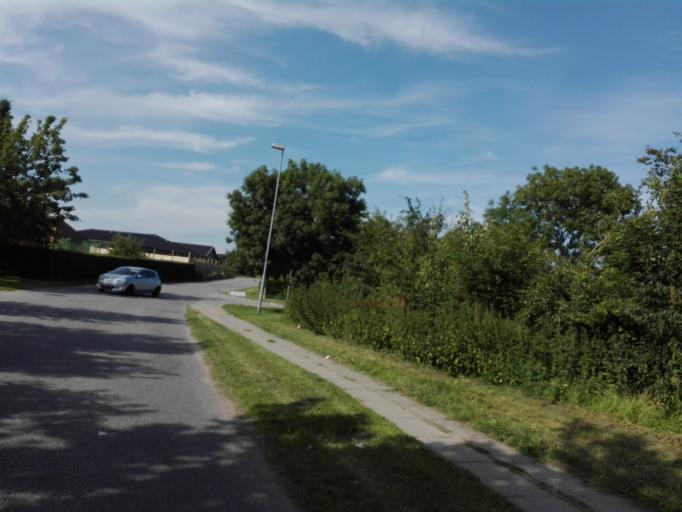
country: DK
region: Central Jutland
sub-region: Arhus Kommune
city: Tranbjerg
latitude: 56.0979
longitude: 10.1295
